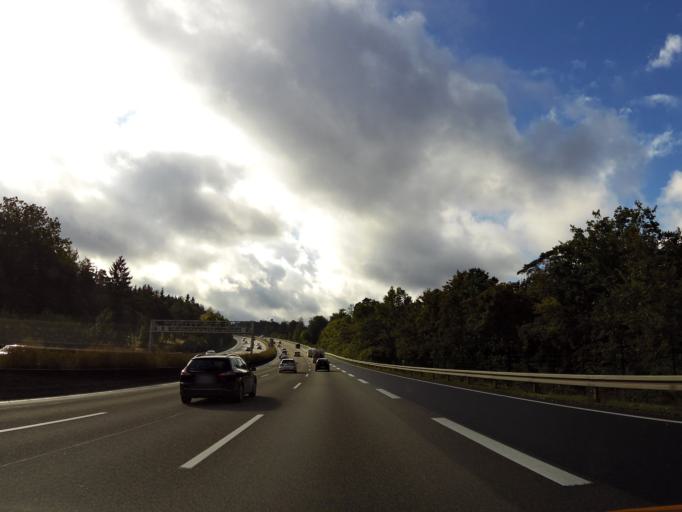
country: DE
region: Hesse
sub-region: Regierungsbezirk Kassel
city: Guxhagen
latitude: 51.1749
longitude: 9.4725
